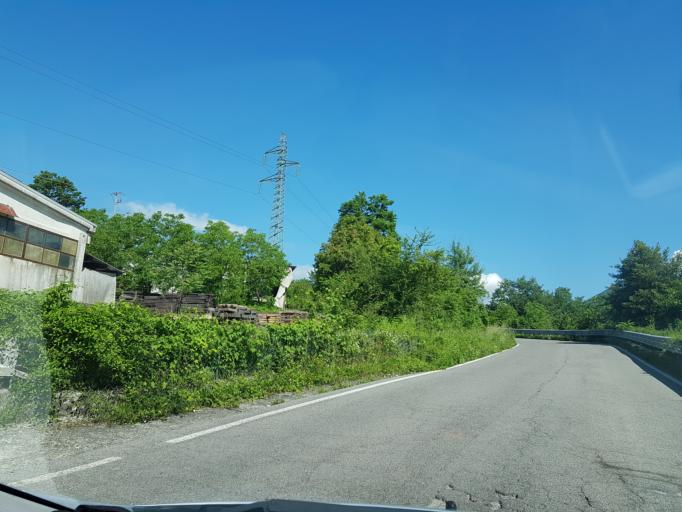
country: IT
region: Tuscany
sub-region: Provincia di Lucca
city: Camporgiano
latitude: 44.1533
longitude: 10.3428
